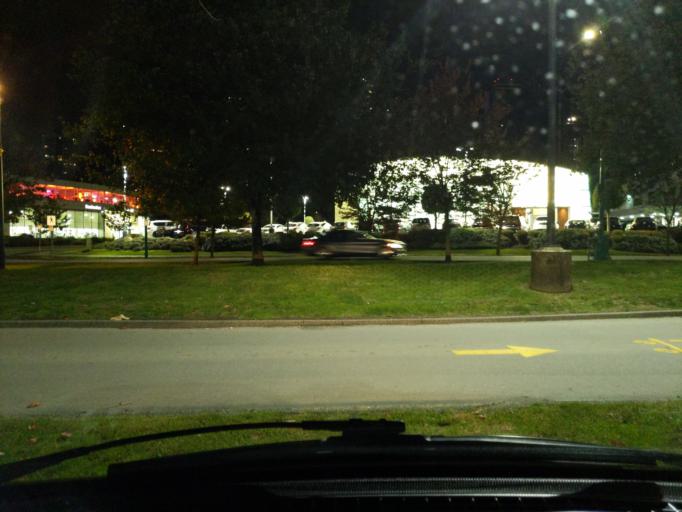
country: CA
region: British Columbia
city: Burnaby
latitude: 49.2606
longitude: -123.0053
